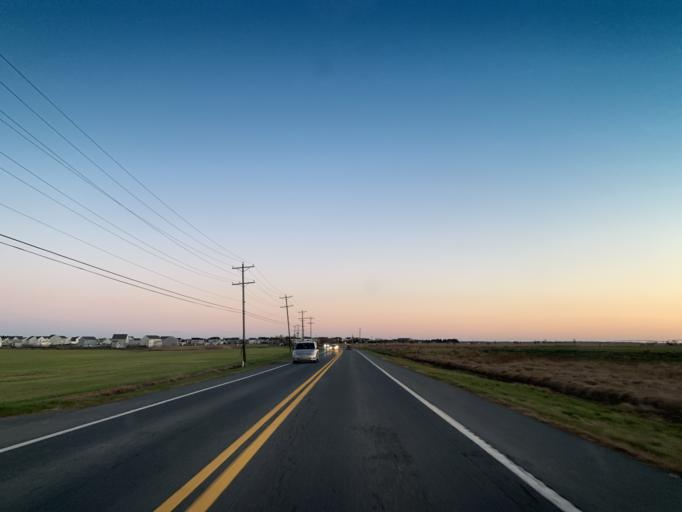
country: US
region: Delaware
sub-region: New Castle County
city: Middletown
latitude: 39.4332
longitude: -75.7434
